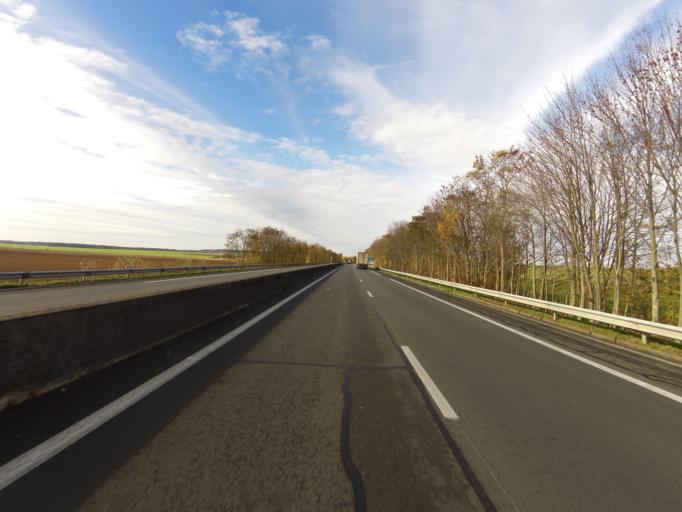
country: FR
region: Picardie
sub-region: Departement de l'Aisne
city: Couvron-et-Aumencourt
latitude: 49.6606
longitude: 3.5454
